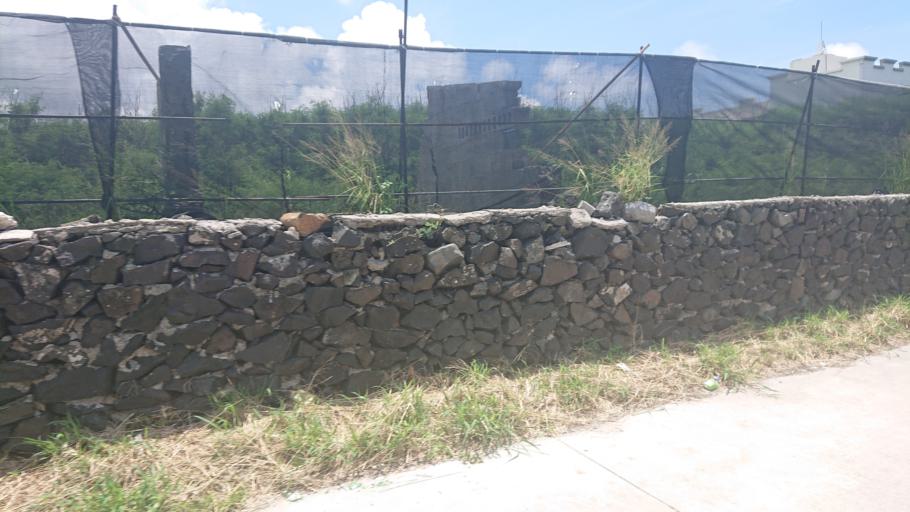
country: TW
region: Taiwan
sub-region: Penghu
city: Ma-kung
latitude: 23.5768
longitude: 119.5786
